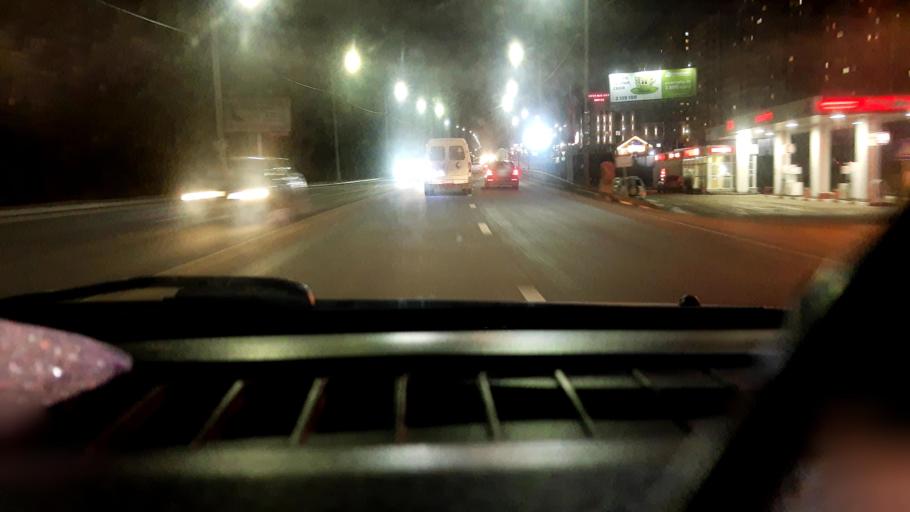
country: RU
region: Nizjnij Novgorod
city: Afonino
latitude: 56.2752
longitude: 44.0803
